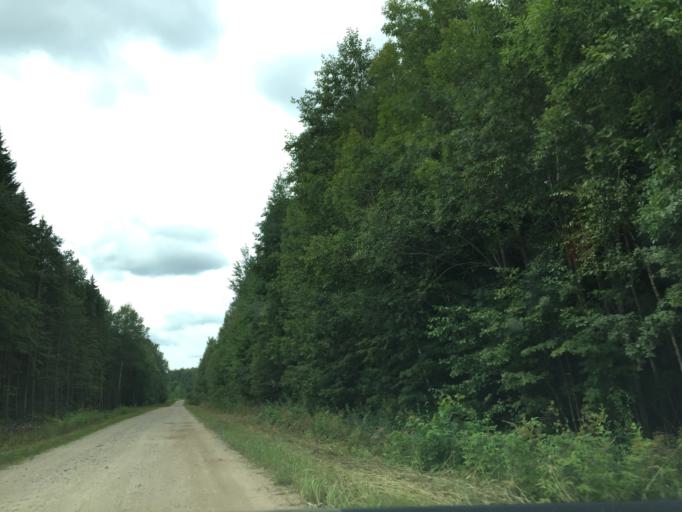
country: LV
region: Lielvarde
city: Lielvarde
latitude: 56.7484
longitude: 24.8809
